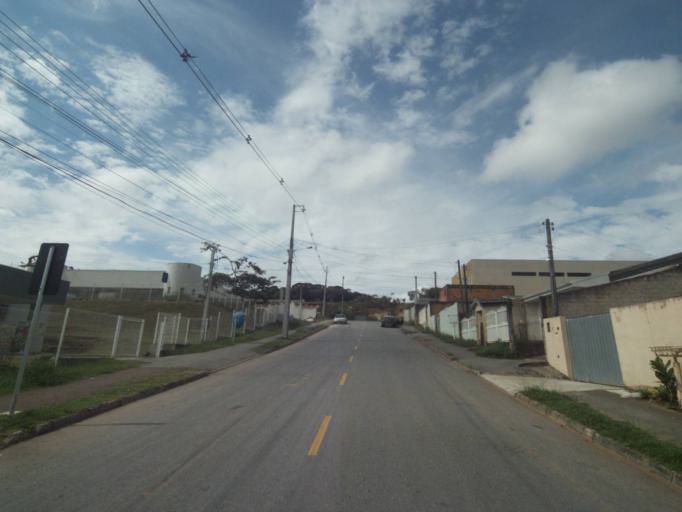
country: BR
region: Parana
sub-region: Quatro Barras
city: Quatro Barras
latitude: -25.3460
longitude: -49.0760
